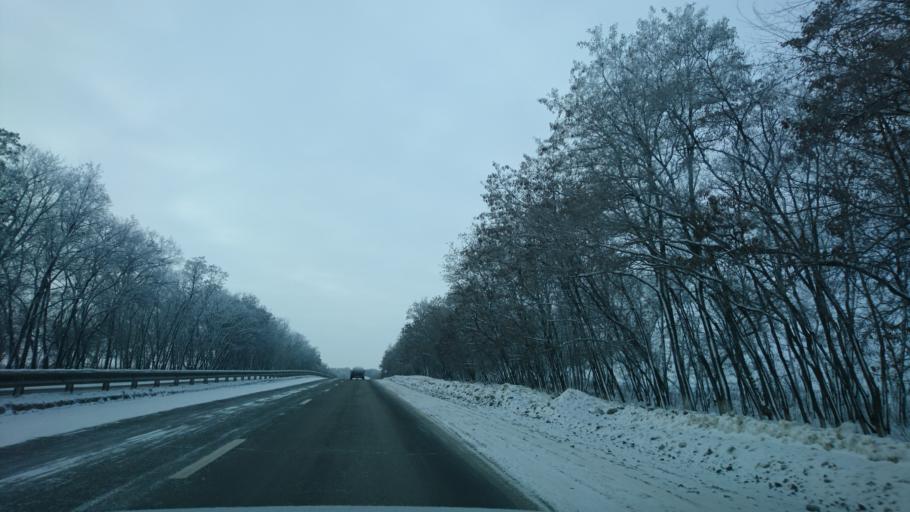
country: RU
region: Belgorod
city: Mayskiy
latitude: 50.4907
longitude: 36.4192
